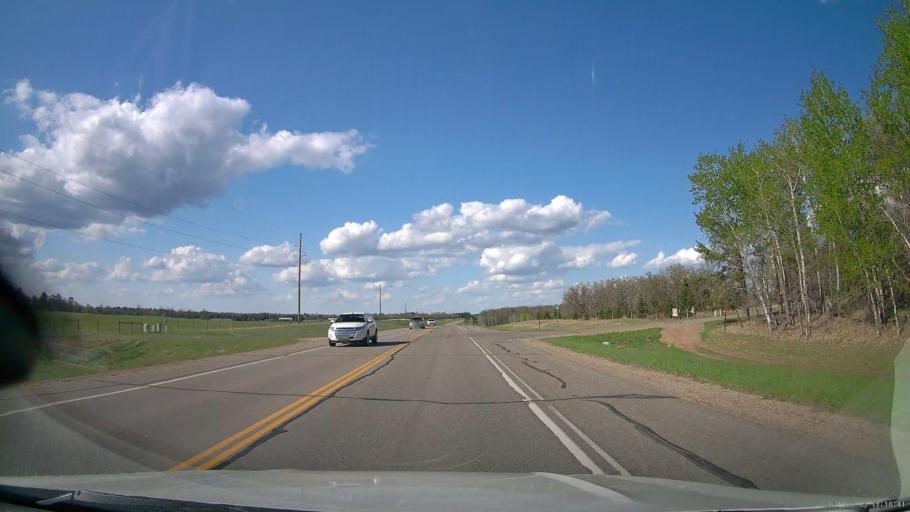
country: US
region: Minnesota
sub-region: Hubbard County
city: Park Rapids
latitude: 46.9652
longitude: -95.0171
